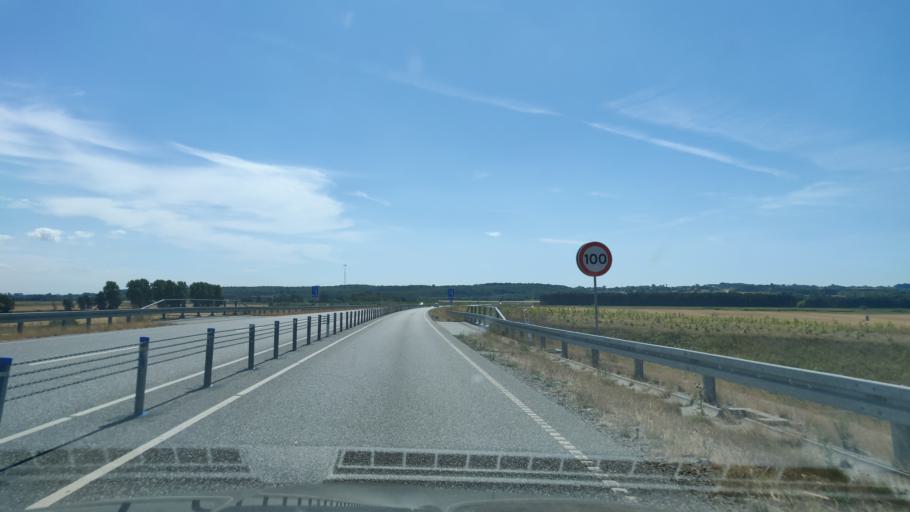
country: DK
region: Zealand
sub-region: Odsherred Kommune
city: Hojby
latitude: 55.8486
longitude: 11.6012
